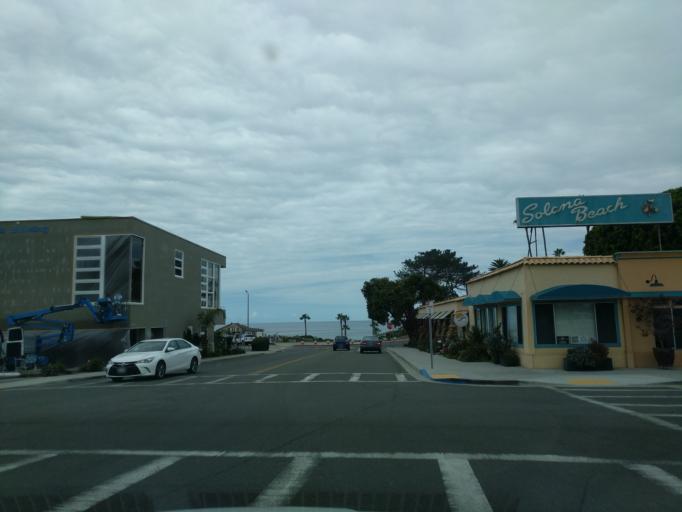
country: US
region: California
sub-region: San Diego County
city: Solana Beach
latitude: 32.9918
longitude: -117.2723
